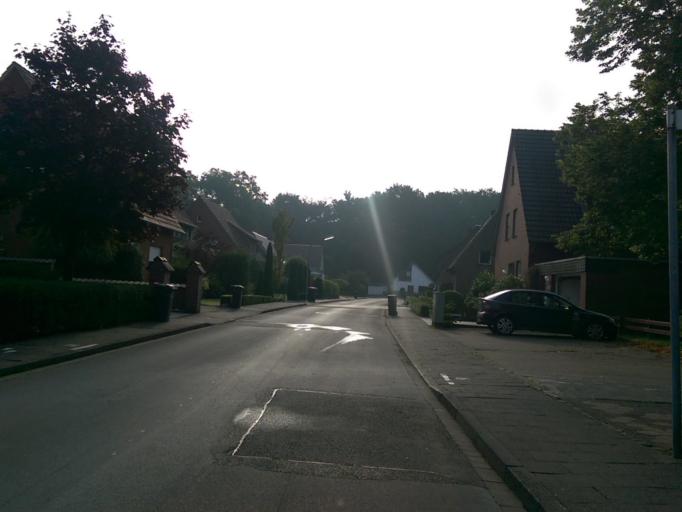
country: DE
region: North Rhine-Westphalia
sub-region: Regierungsbezirk Detmold
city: Harsewinkel
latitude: 51.9507
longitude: 8.2819
